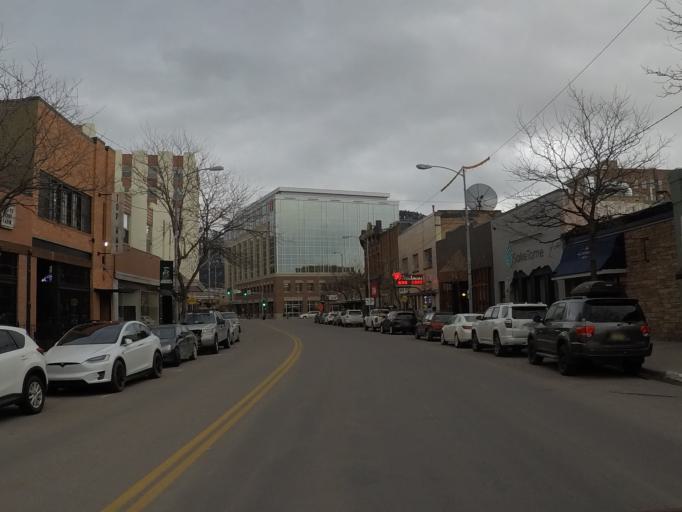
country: US
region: Montana
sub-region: Missoula County
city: Missoula
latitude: 46.8707
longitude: -113.9966
